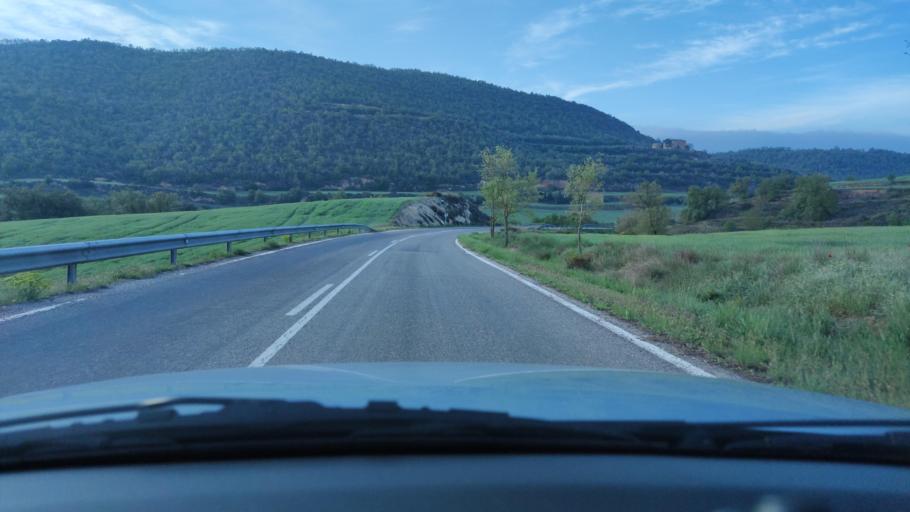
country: ES
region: Catalonia
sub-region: Provincia de Lleida
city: Ponts
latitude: 41.8892
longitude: 1.1833
